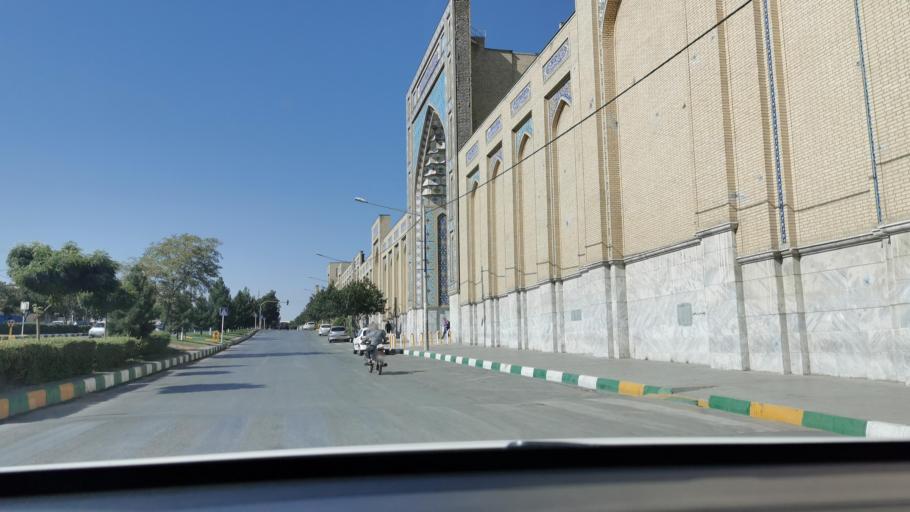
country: IR
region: Razavi Khorasan
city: Mashhad
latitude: 36.3433
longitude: 59.6323
